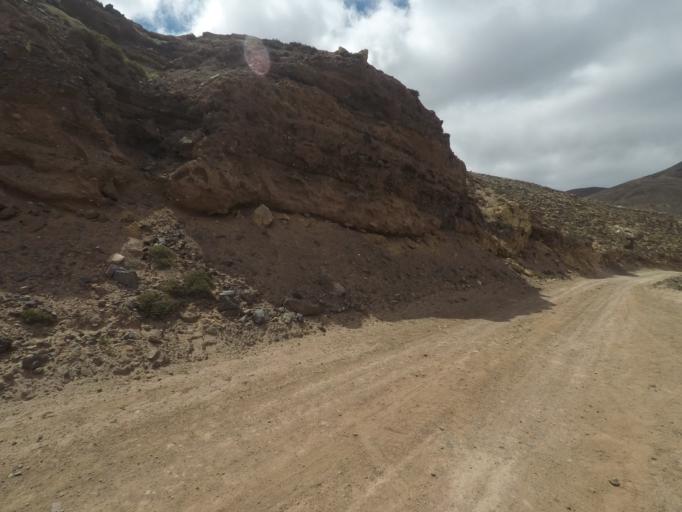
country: PT
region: Madeira
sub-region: Porto Santo
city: Vila de Porto Santo
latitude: 33.0658
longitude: -16.2969
